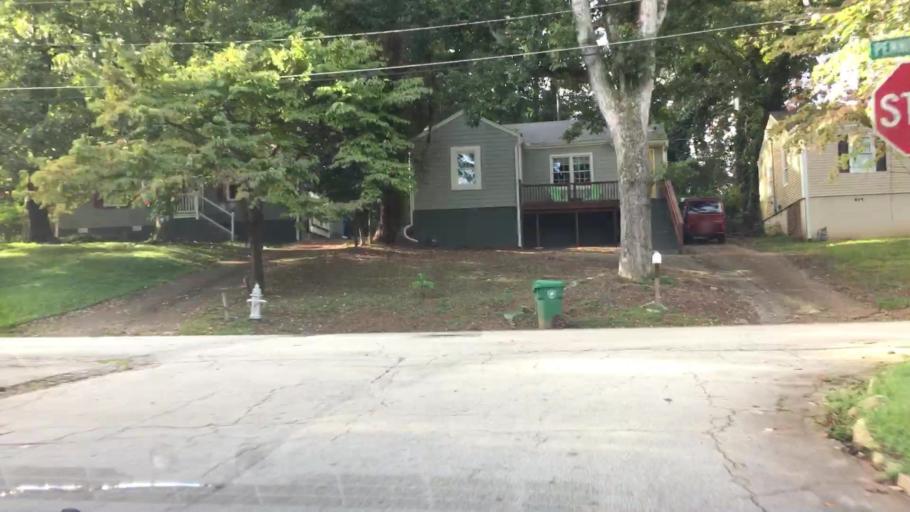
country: US
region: Georgia
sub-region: DeKalb County
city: Gresham Park
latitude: 33.7383
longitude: -84.3183
